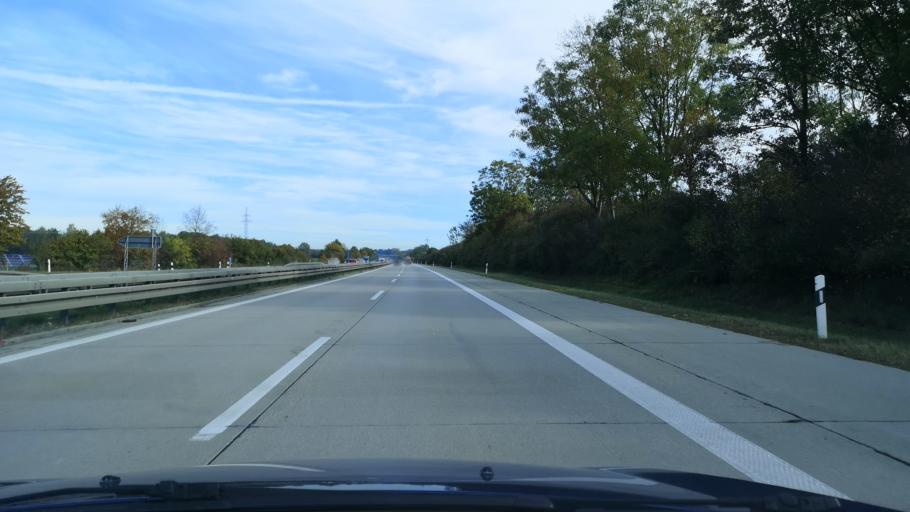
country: DE
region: Bavaria
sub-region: Upper Bavaria
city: Forstinning
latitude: 48.1707
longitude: 11.8925
